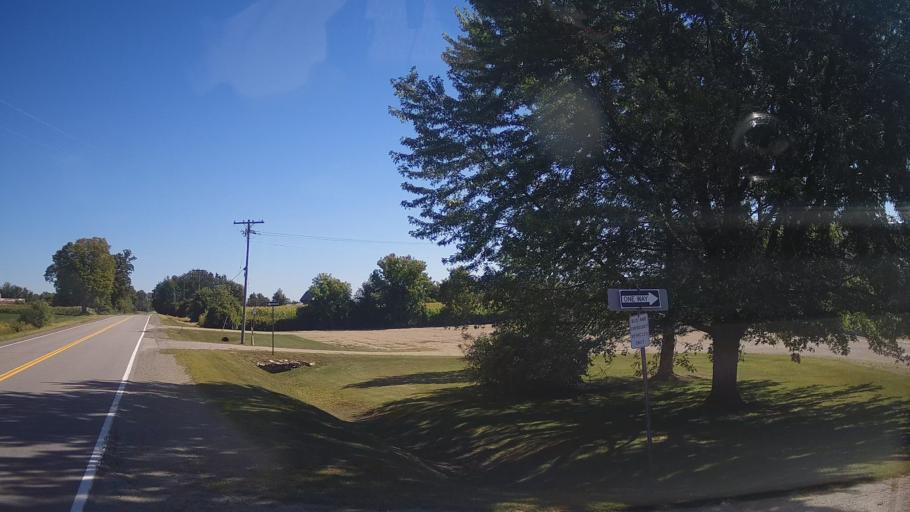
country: CA
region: Ontario
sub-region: Lanark County
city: Smiths Falls
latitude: 44.8471
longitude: -75.8701
